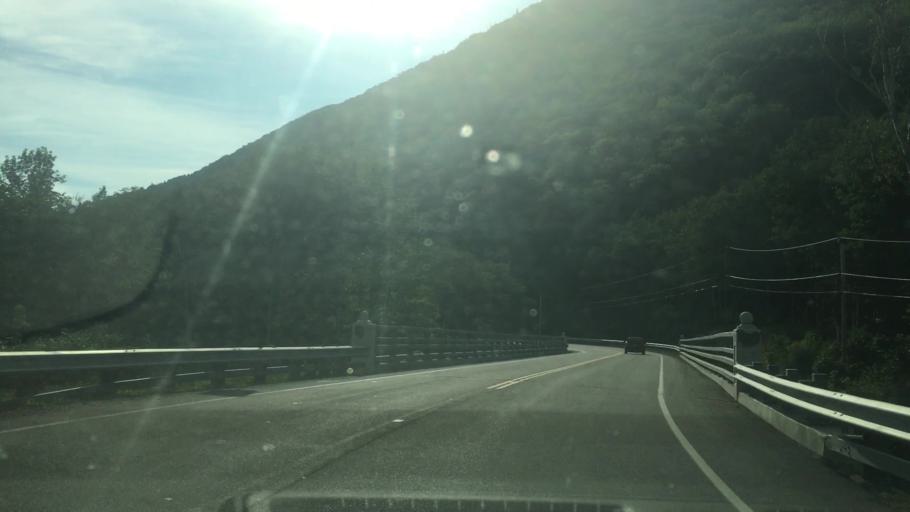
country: CA
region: Nova Scotia
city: Sydney Mines
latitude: 46.8279
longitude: -60.6187
